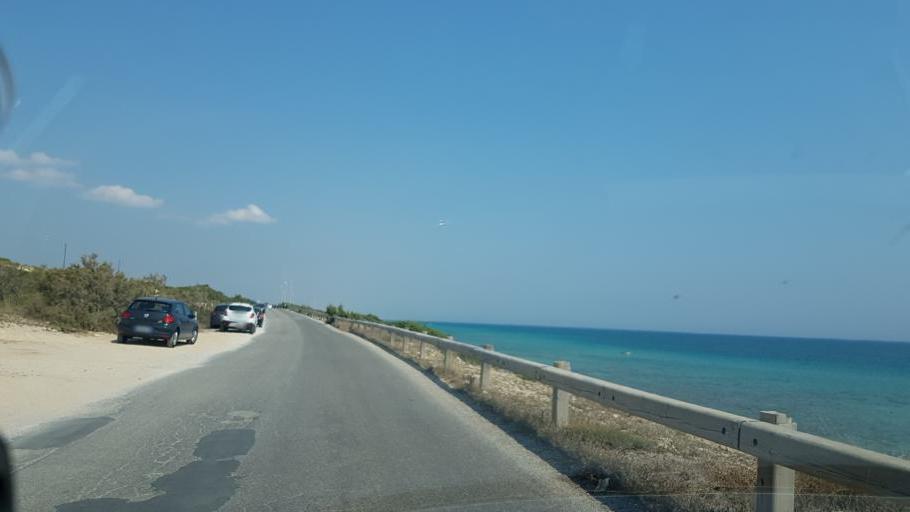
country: IT
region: Apulia
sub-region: Provincia di Taranto
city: Maruggio
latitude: 40.2999
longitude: 17.5972
